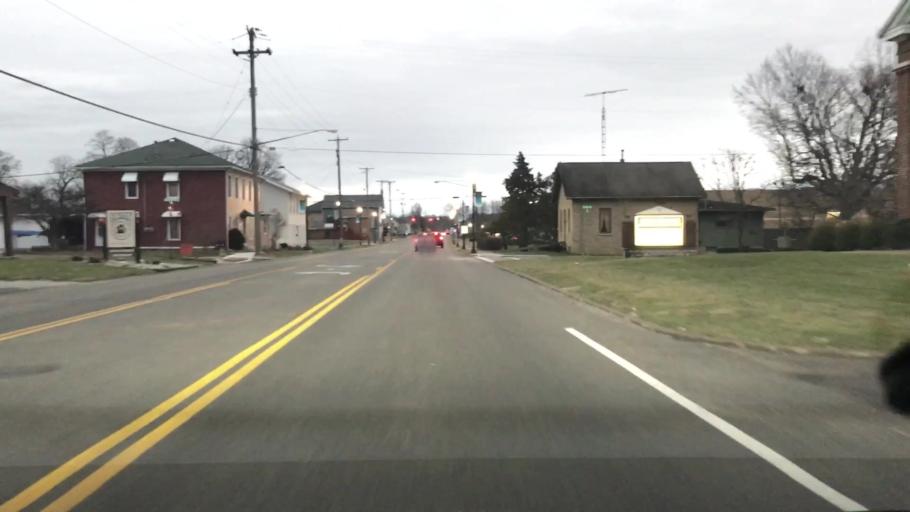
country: US
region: Ohio
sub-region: Clark County
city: Enon
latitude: 39.8772
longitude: -83.9392
